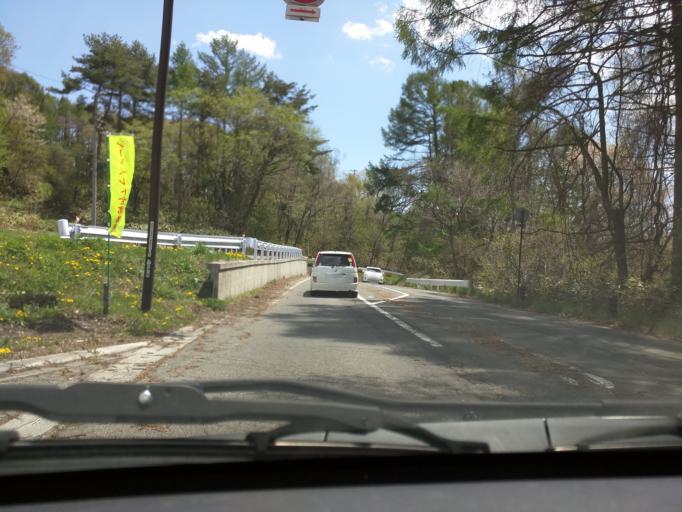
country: JP
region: Nagano
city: Nagano-shi
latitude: 36.7016
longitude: 138.1518
